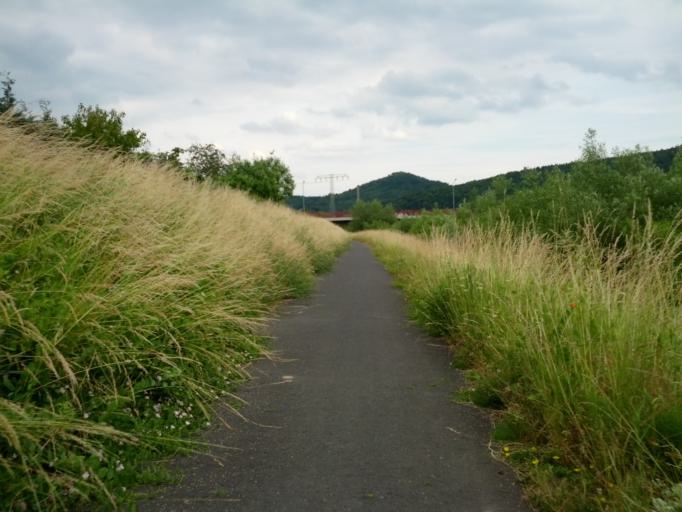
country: DE
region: Thuringia
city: Eisenach
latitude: 50.9835
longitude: 10.2843
